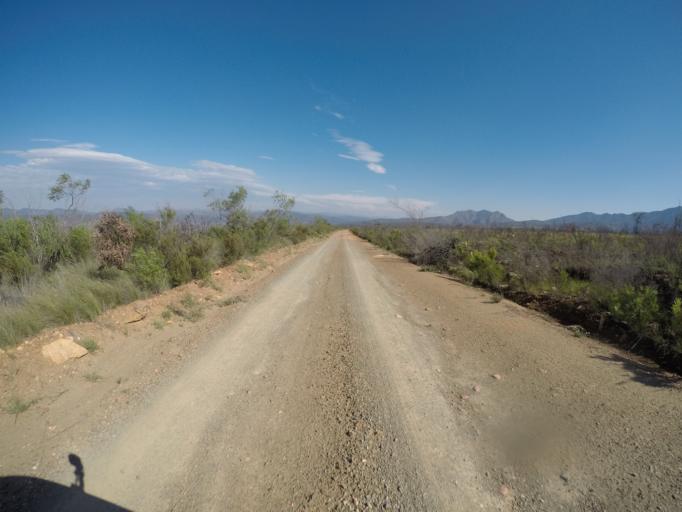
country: ZA
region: Eastern Cape
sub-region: Cacadu District Municipality
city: Kareedouw
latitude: -33.6352
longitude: 24.4681
